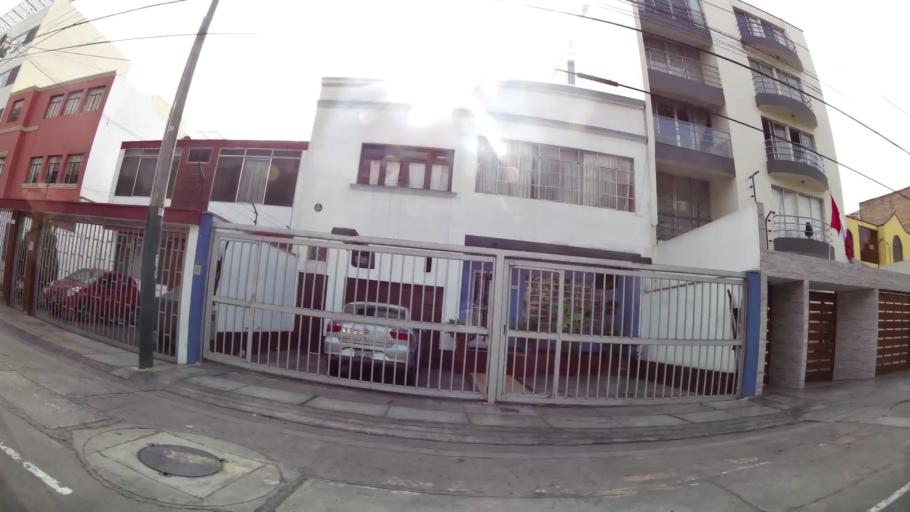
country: PE
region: Lima
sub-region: Lima
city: San Isidro
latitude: -12.0895
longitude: -77.0629
